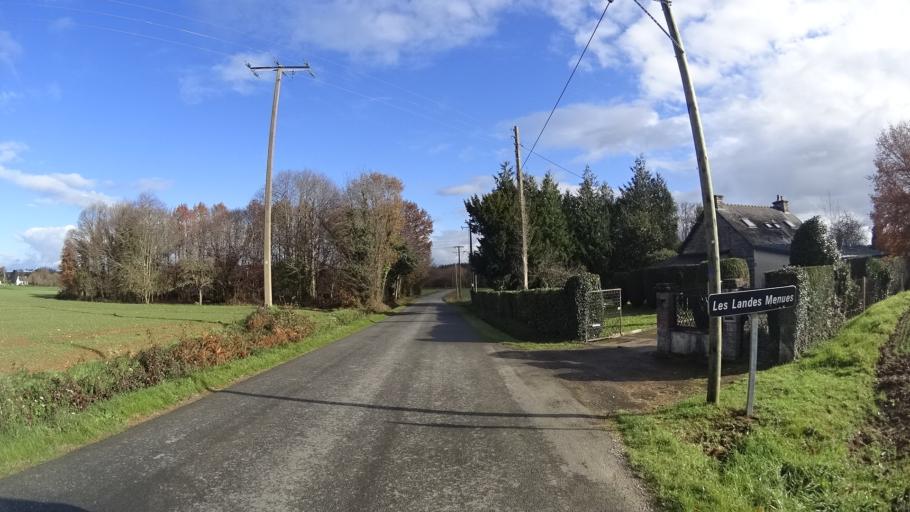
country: FR
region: Brittany
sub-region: Departement du Morbihan
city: Carentoir
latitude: 47.8217
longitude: -2.1198
